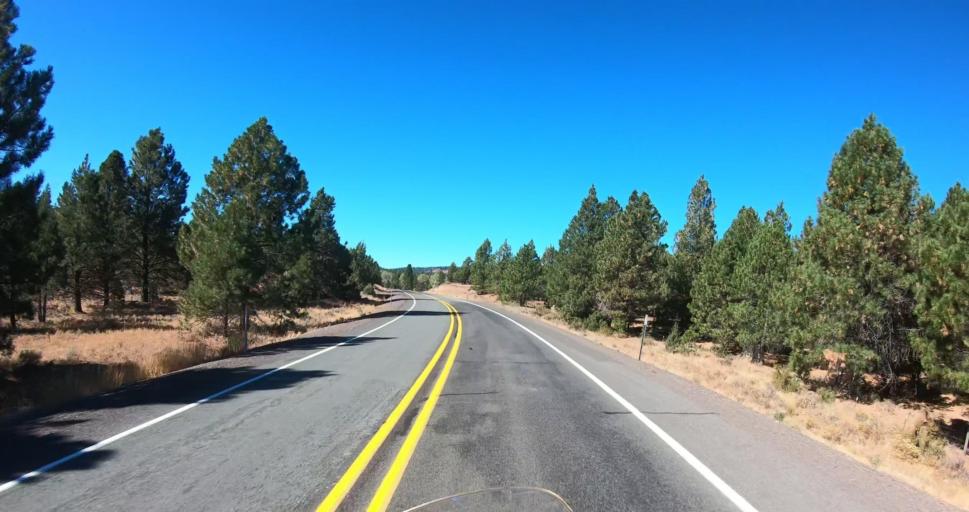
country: US
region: Oregon
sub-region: Lake County
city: Lakeview
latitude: 42.2271
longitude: -120.2456
